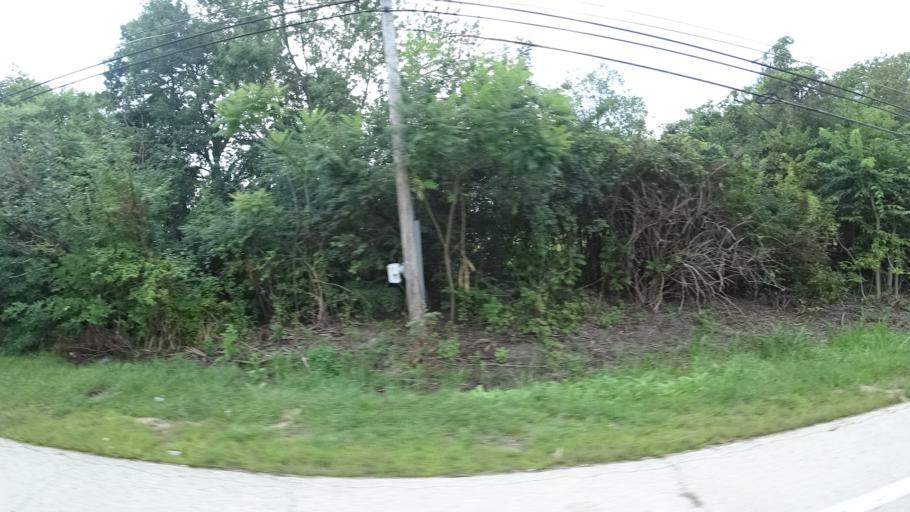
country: US
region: Illinois
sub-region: Will County
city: Goodings Grove
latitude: 41.6566
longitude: -87.8929
